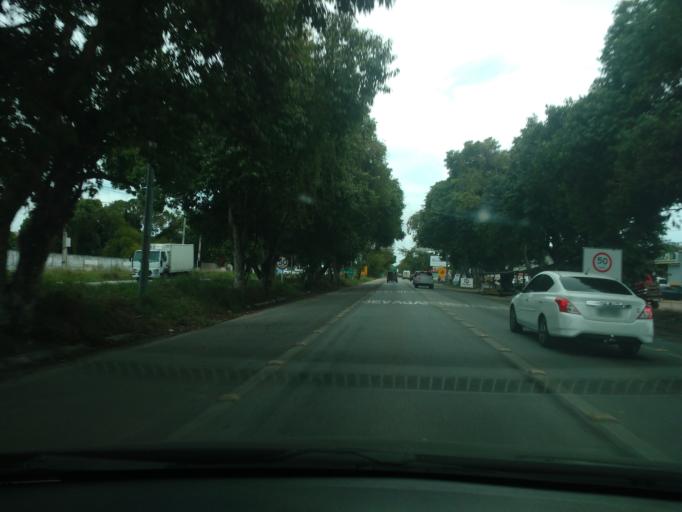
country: BR
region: Alagoas
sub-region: Satuba
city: Satuba
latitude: -9.5171
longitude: -35.8038
